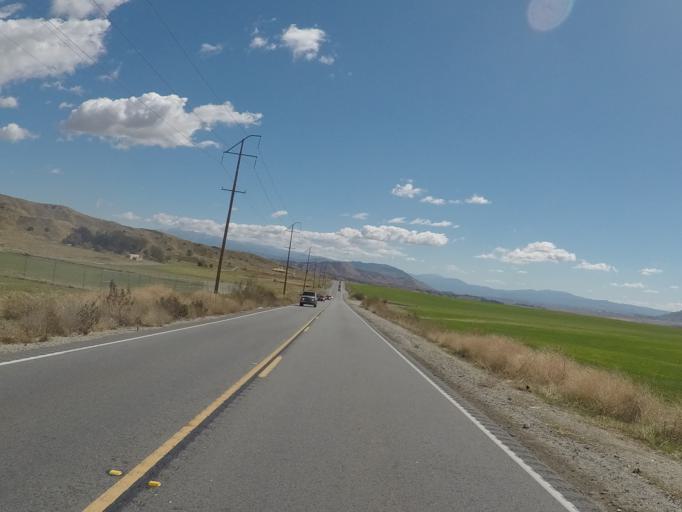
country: US
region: California
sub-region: Riverside County
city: Lakeview
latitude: 33.9270
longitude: -117.1186
